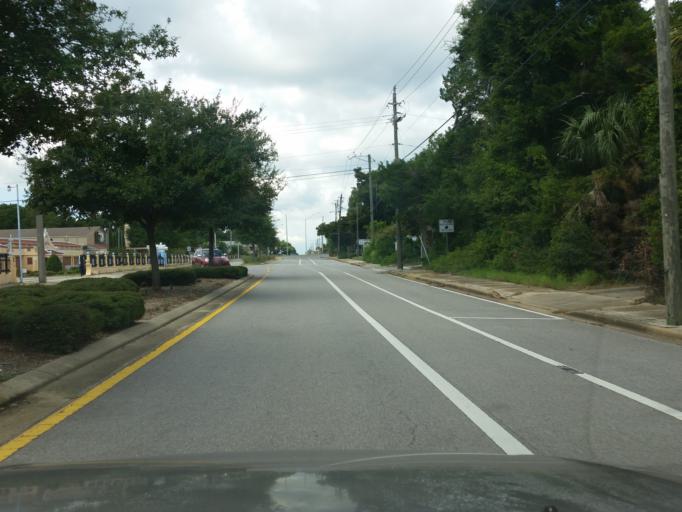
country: US
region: Florida
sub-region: Escambia County
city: Warrington
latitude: 30.3957
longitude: -87.2498
